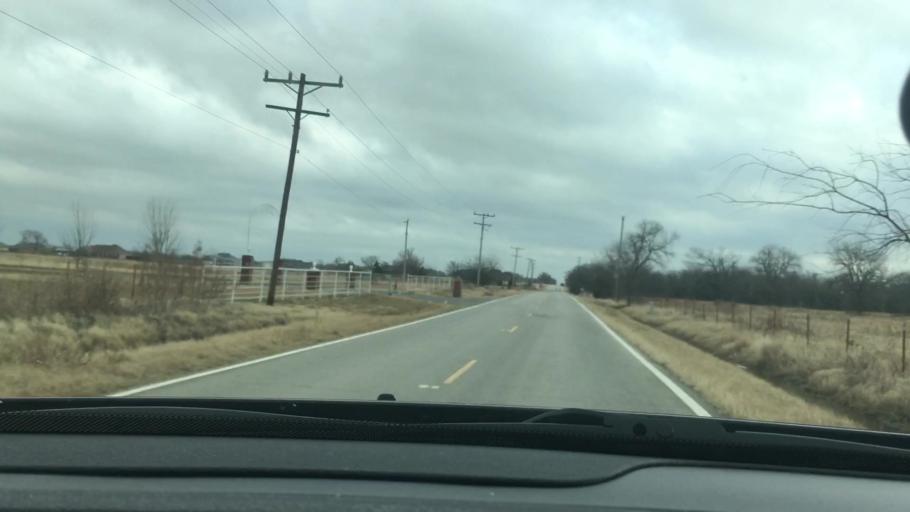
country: US
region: Oklahoma
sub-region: Bryan County
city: Durant
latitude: 34.0848
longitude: -96.4295
